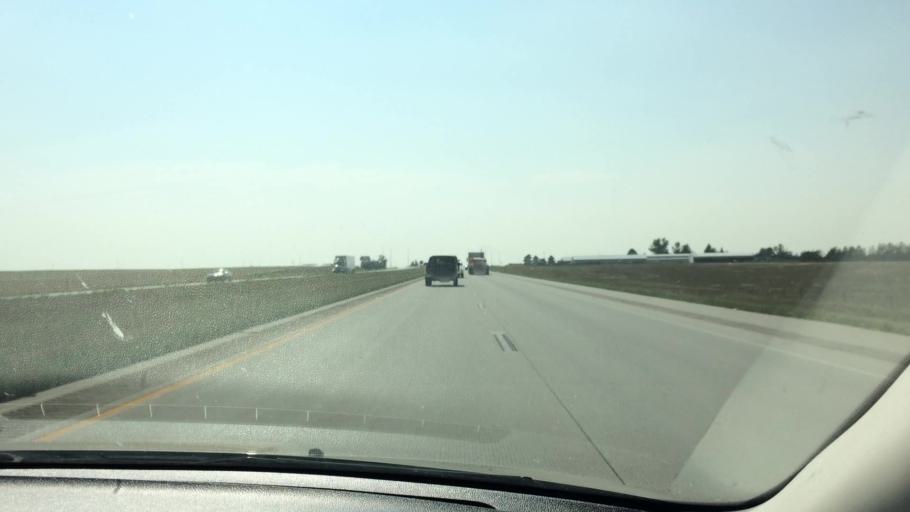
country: US
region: Colorado
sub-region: Adams County
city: Bennett
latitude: 39.7388
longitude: -104.5175
